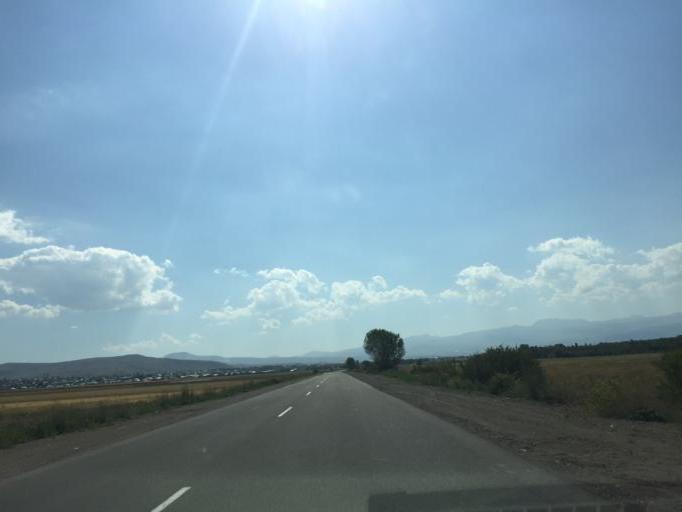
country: AM
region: Geghark'unik'i Marz
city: Vardenik
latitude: 40.1460
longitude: 45.3964
